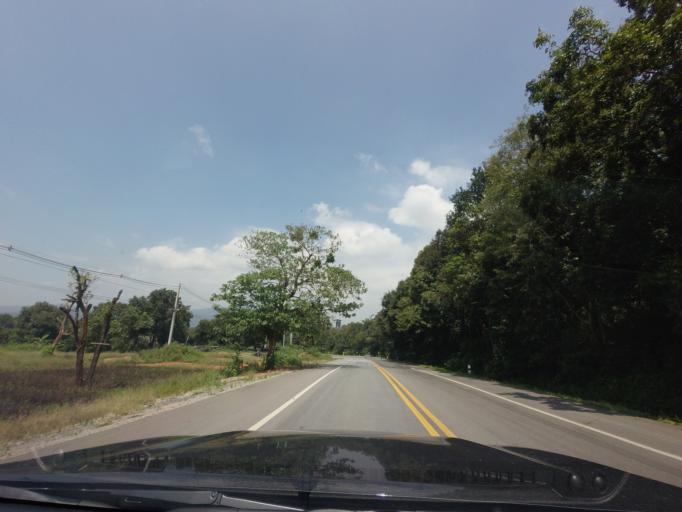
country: TH
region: Loei
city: Phu Ruea
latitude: 17.4581
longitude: 101.4143
